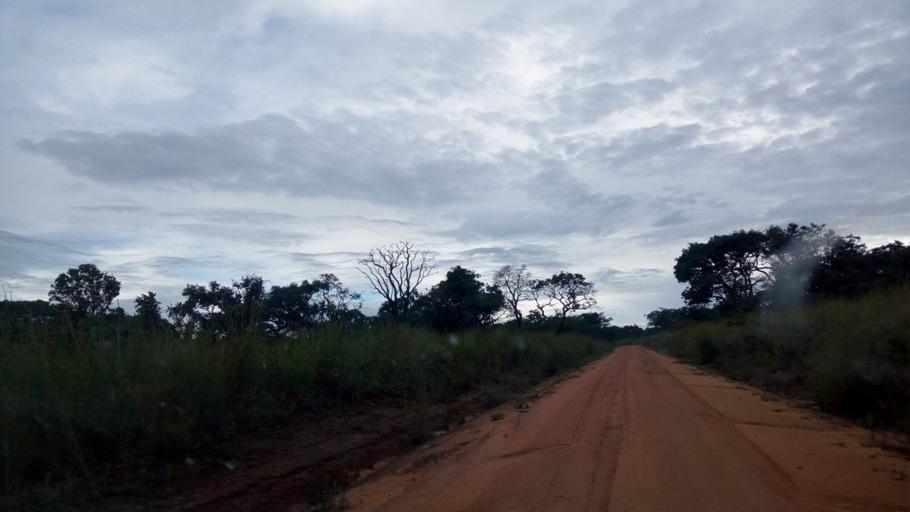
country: CD
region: Katanga
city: Kalemie
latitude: -6.7386
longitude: 29.1081
